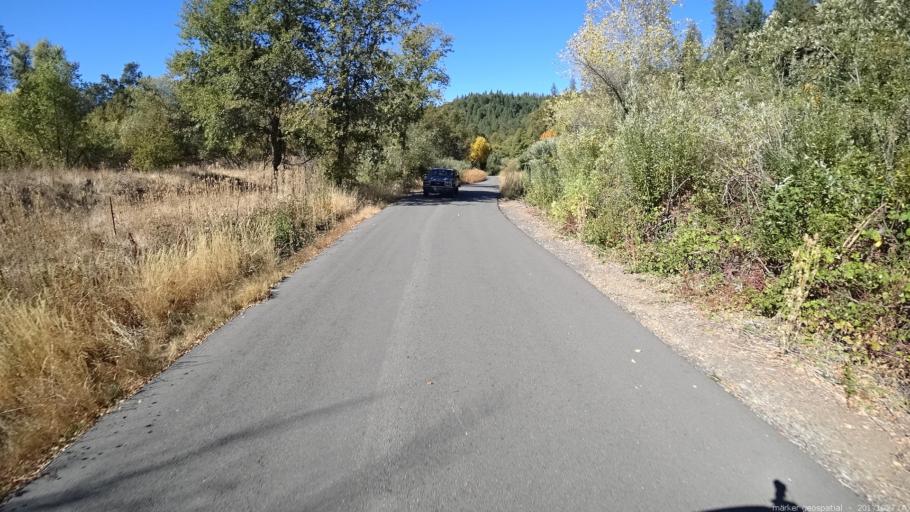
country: US
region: California
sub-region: Shasta County
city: Bella Vista
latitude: 40.7544
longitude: -122.0231
